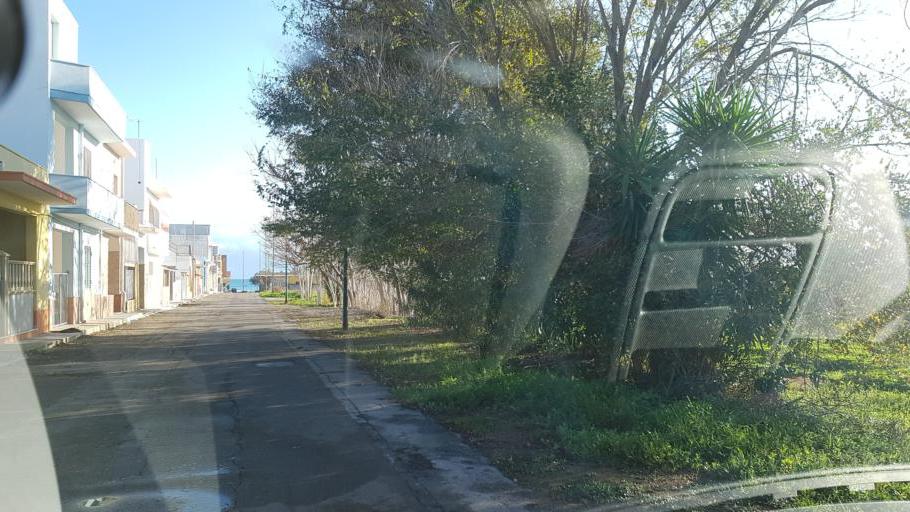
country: IT
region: Apulia
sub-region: Provincia di Brindisi
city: Torchiarolo
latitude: 40.5342
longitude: 18.0726
